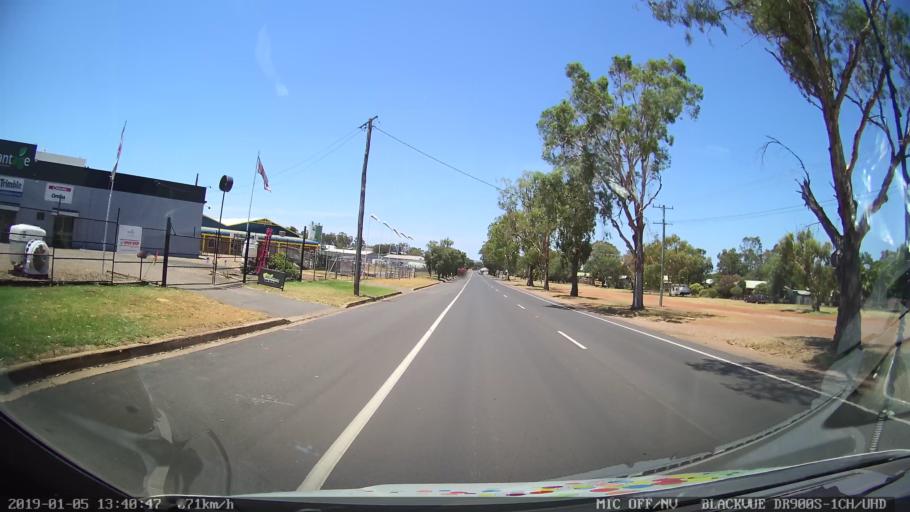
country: AU
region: New South Wales
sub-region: Gunnedah
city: Gunnedah
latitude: -30.9805
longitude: 150.2333
